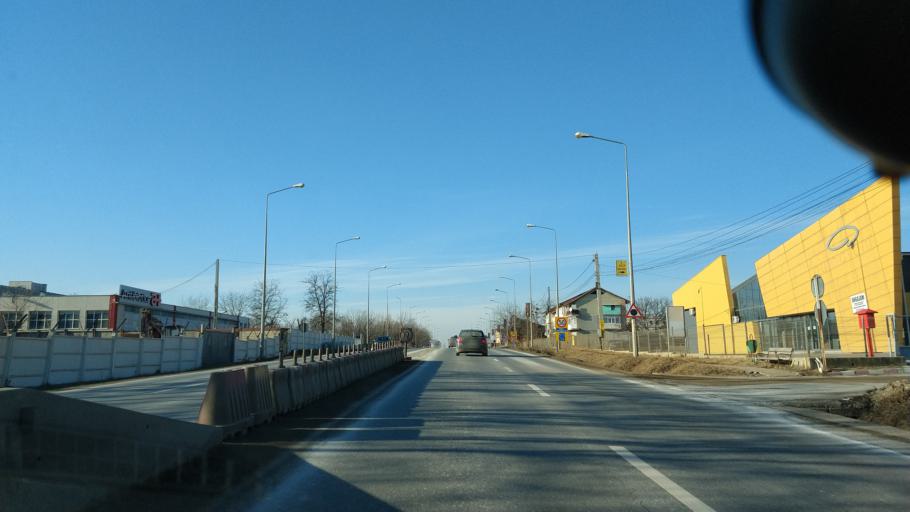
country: RO
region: Iasi
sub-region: Comuna Valea Lupului
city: Valea Lupului
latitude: 47.1764
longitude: 27.4934
